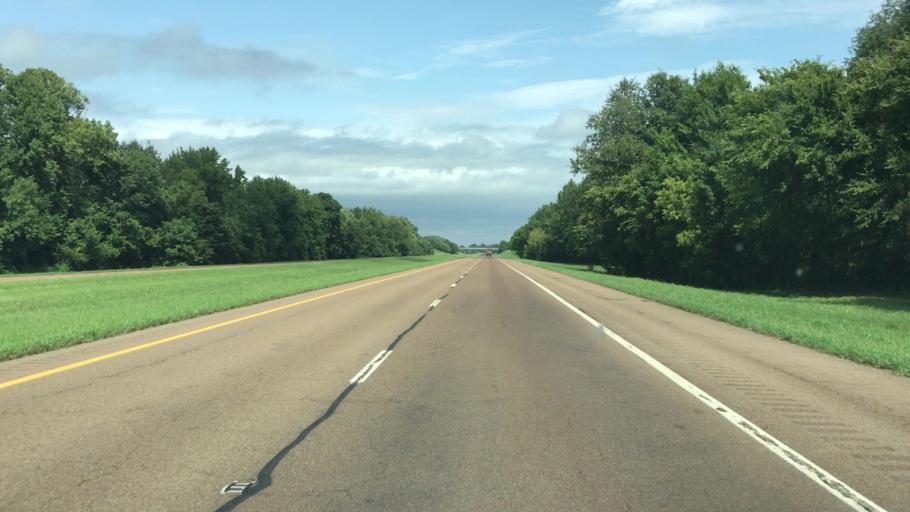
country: US
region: Tennessee
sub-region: Obion County
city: South Fulton
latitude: 36.4846
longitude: -88.9358
